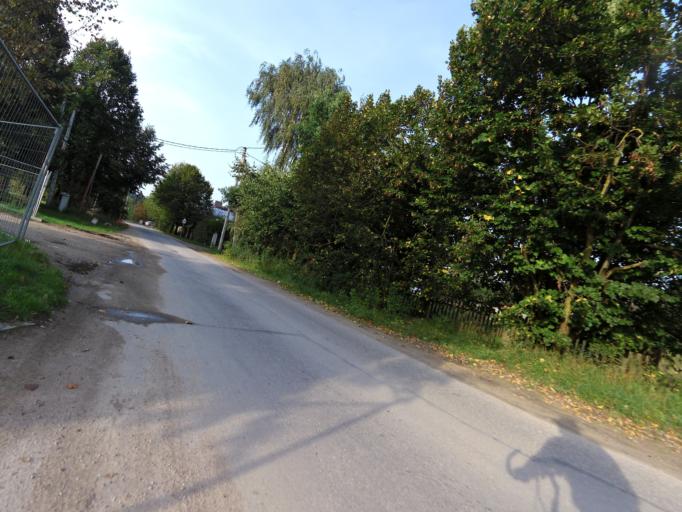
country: LT
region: Vilnius County
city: Vilkpede
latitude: 54.6801
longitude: 25.2270
